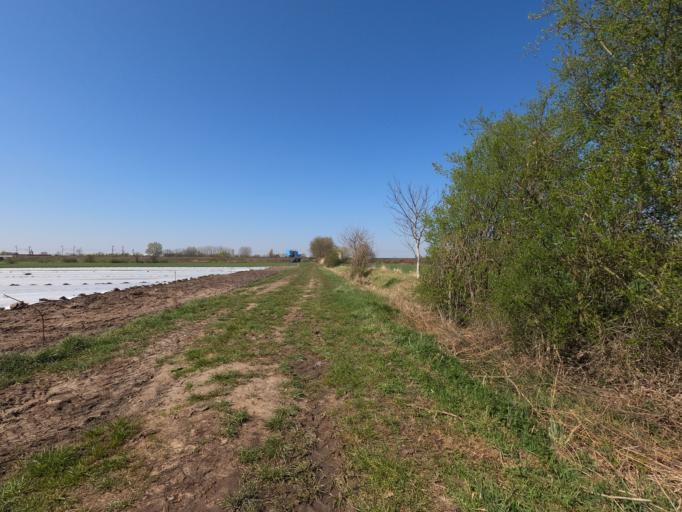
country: DE
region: Hesse
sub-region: Regierungsbezirk Darmstadt
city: Gross-Gerau
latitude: 49.9268
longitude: 8.5092
